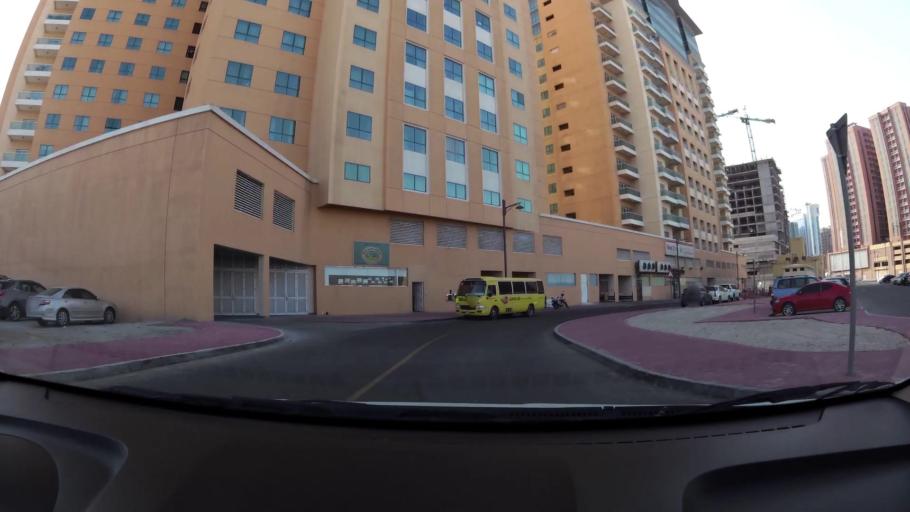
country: AE
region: Ash Shariqah
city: Sharjah
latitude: 25.2892
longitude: 55.3568
